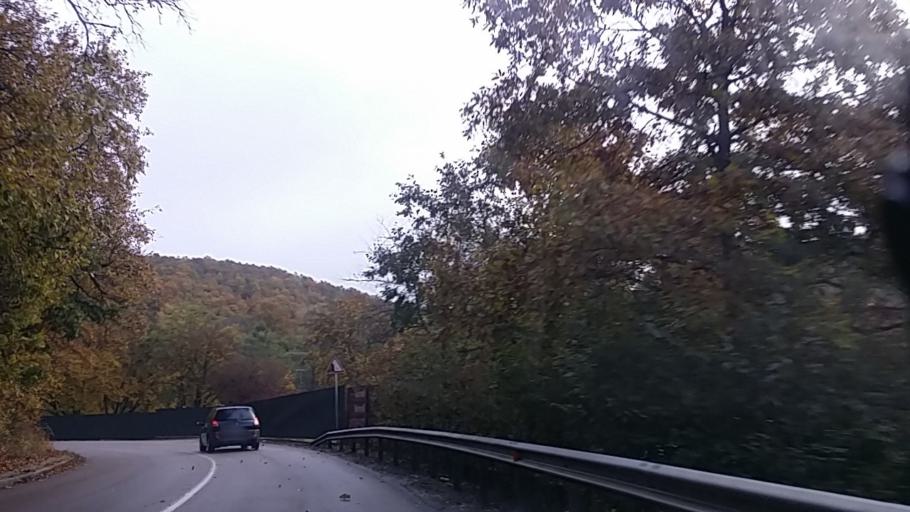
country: HU
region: Heves
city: Belapatfalva
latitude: 47.9816
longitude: 20.3437
